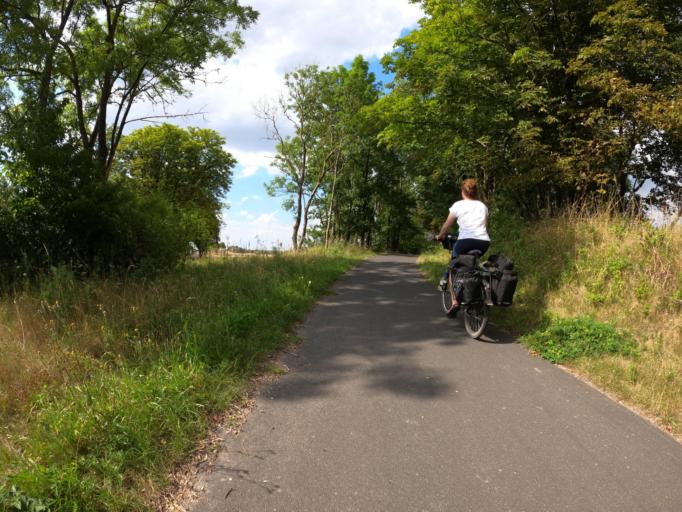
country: DE
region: Mecklenburg-Vorpommern
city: Woldegk
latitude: 53.3825
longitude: 13.5891
